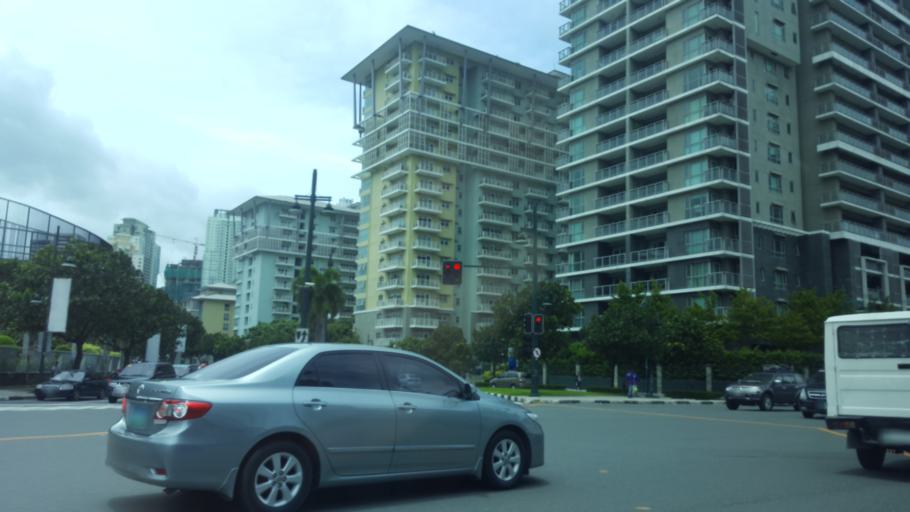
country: PH
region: Calabarzon
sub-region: Province of Rizal
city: Pateros
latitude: 14.5520
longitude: 121.0561
